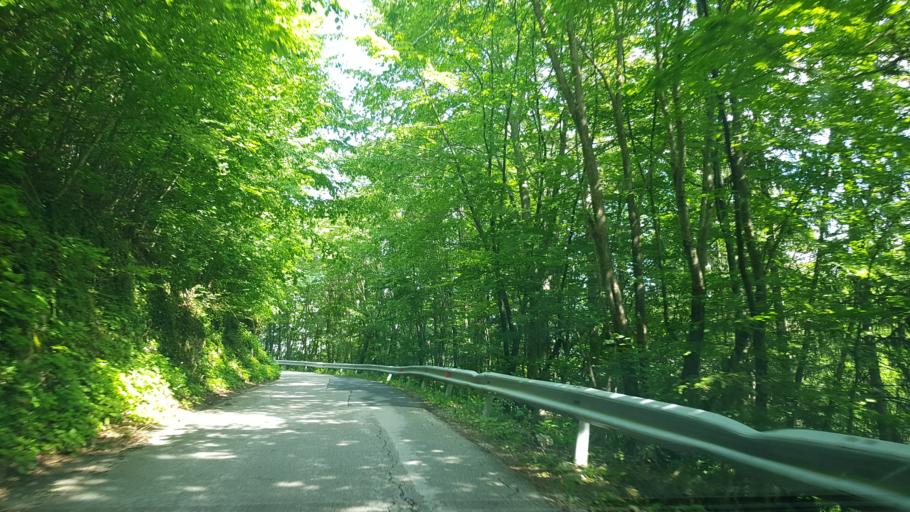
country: SI
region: Velenje
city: Velenje
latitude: 46.3846
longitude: 15.1705
